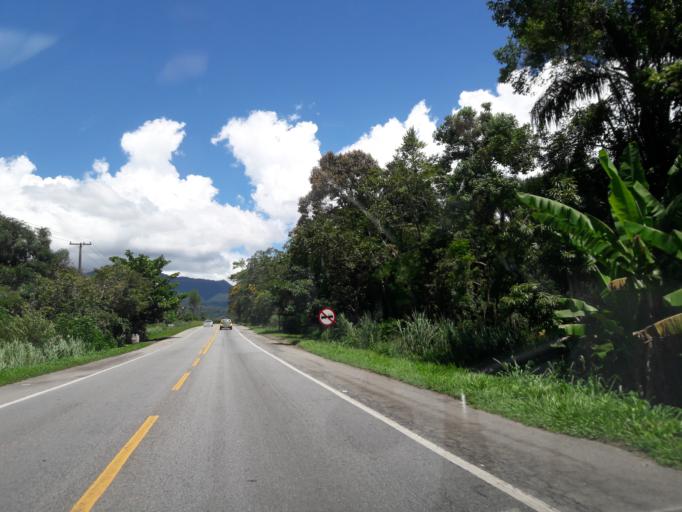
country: BR
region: Parana
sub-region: Antonina
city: Antonina
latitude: -25.5328
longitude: -48.7942
